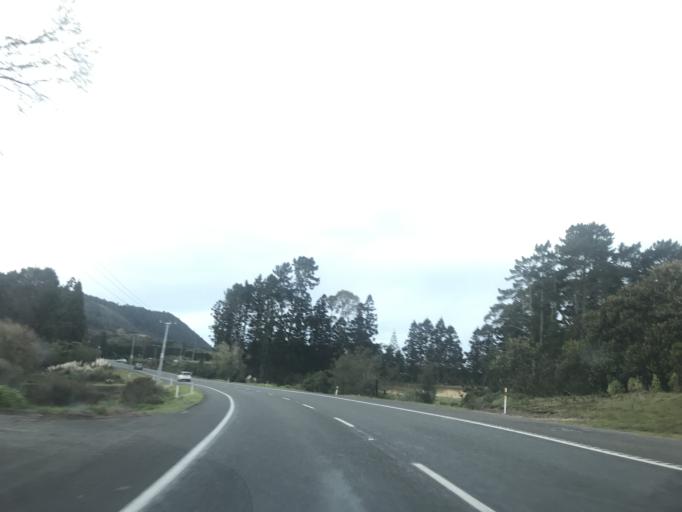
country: NZ
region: Bay of Plenty
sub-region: Western Bay of Plenty District
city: Katikati
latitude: -37.4837
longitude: 175.9309
